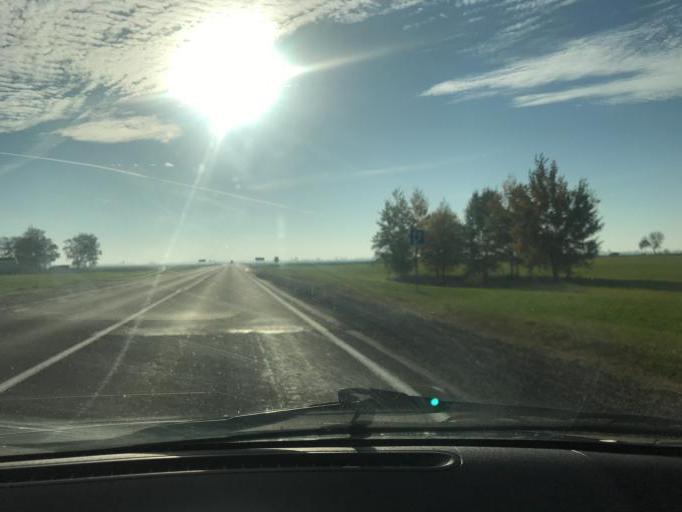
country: BY
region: Brest
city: Drahichyn
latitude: 52.2046
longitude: 25.2260
